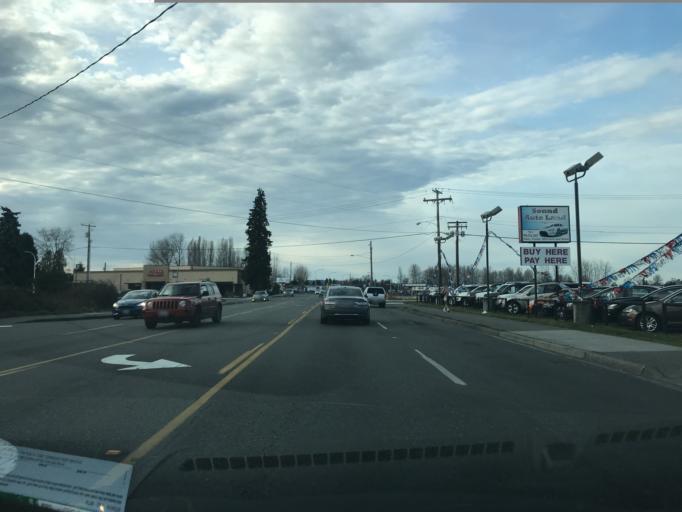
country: US
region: Washington
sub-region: King County
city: Kent
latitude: 47.3506
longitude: -122.2264
